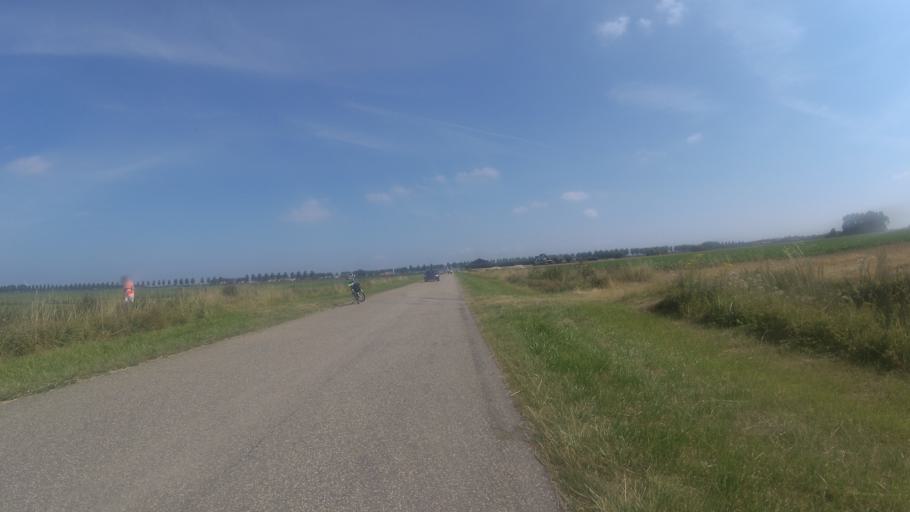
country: NL
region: Zeeland
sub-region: Gemeente Noord-Beveland
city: Kamperland
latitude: 51.5522
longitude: 3.7250
